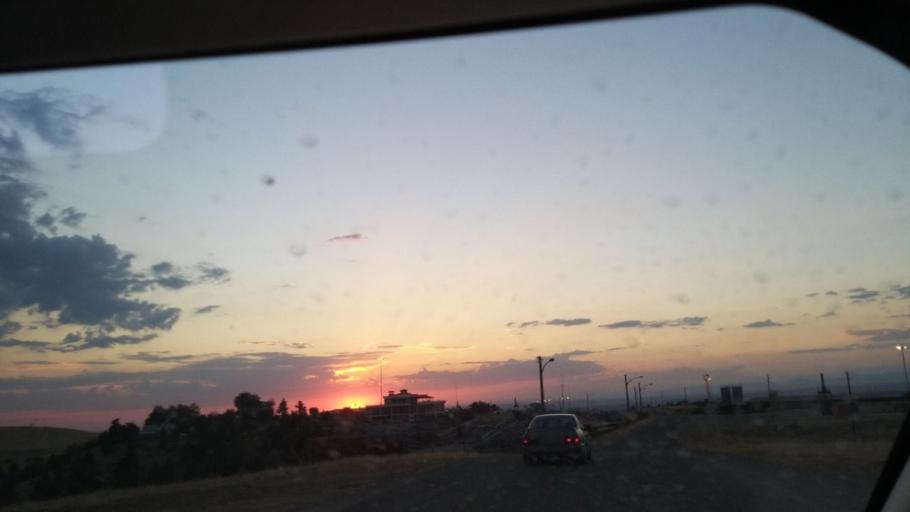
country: TR
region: Batman
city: Erkoklu
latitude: 37.8100
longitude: 41.1279
